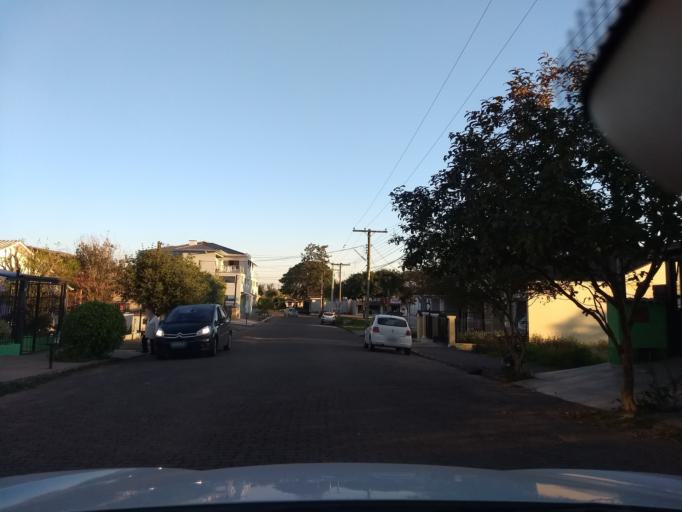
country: BR
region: Rio Grande do Sul
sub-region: Santa Cruz Do Sul
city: Santa Cruz do Sul
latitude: -29.7144
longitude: -52.5069
